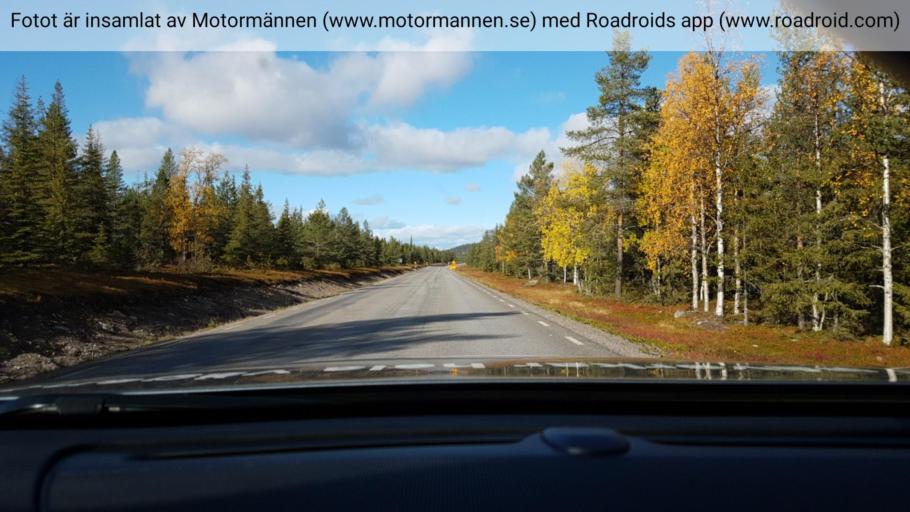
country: SE
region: Norrbotten
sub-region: Arjeplogs Kommun
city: Arjeplog
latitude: 65.9096
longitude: 18.3466
